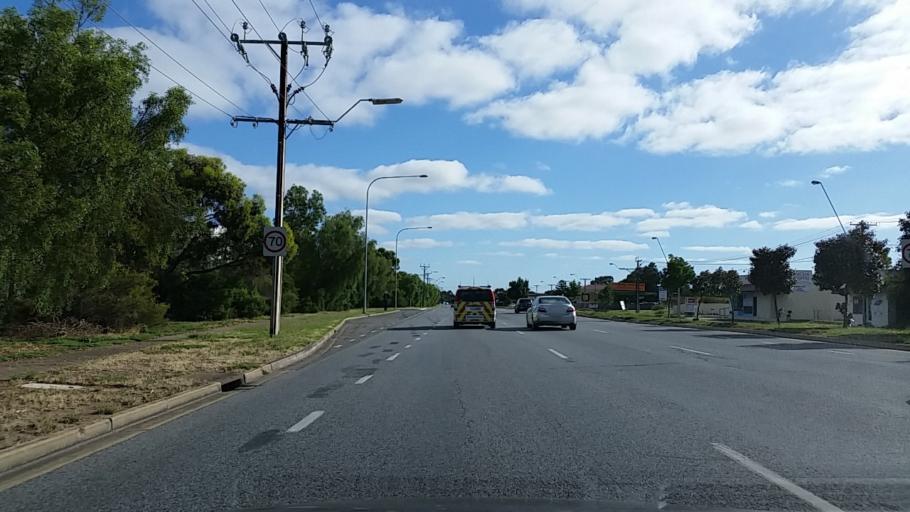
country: AU
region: South Australia
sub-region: Salisbury
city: Ingle Farm
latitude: -34.8314
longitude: 138.6121
